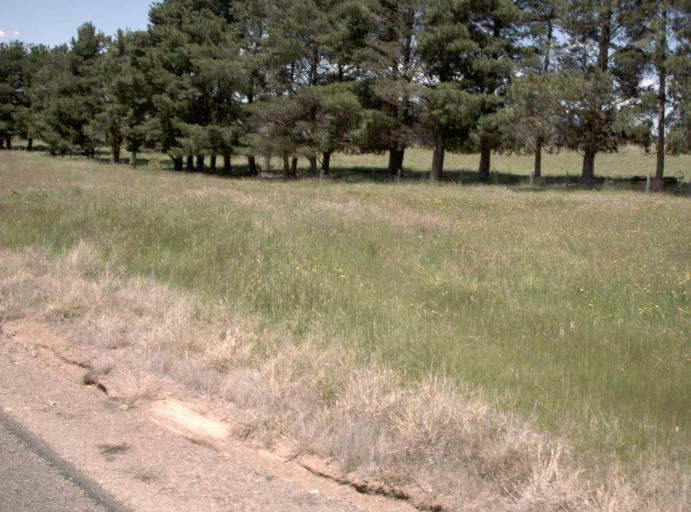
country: AU
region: New South Wales
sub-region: Snowy River
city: Jindabyne
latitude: -37.0810
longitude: 148.2790
